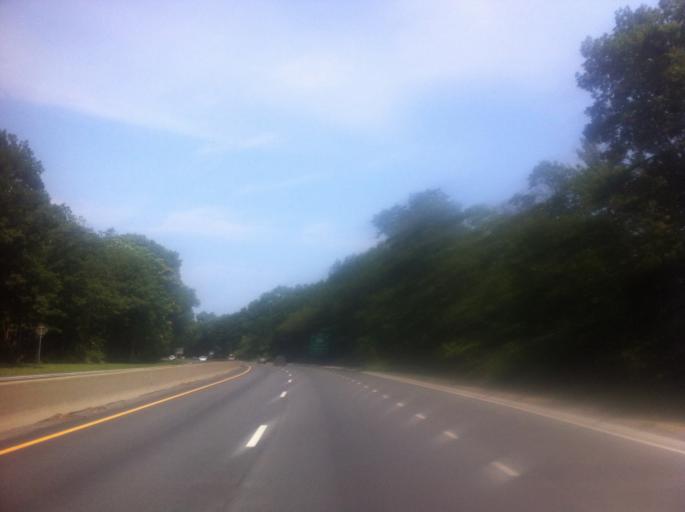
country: US
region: New York
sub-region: Nassau County
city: Hicksville
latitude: 40.7915
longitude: -73.5101
